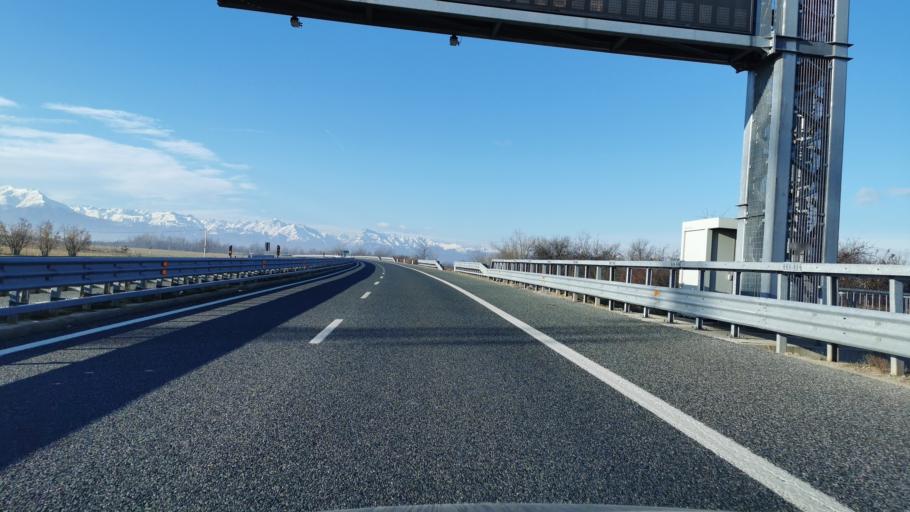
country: IT
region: Piedmont
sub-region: Provincia di Cuneo
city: Magliano Alpi
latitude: 44.4832
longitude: 7.8005
